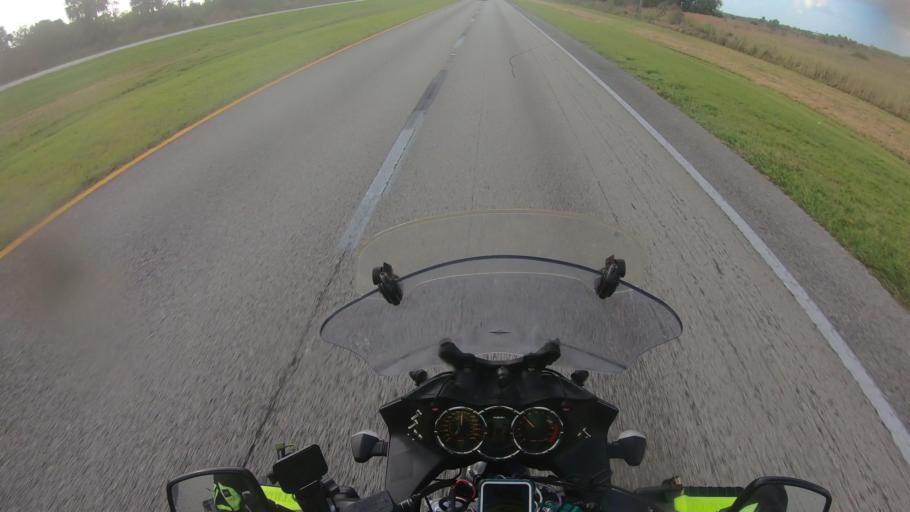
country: US
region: Florida
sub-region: Glades County
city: Moore Haven
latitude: 26.9030
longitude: -81.2597
